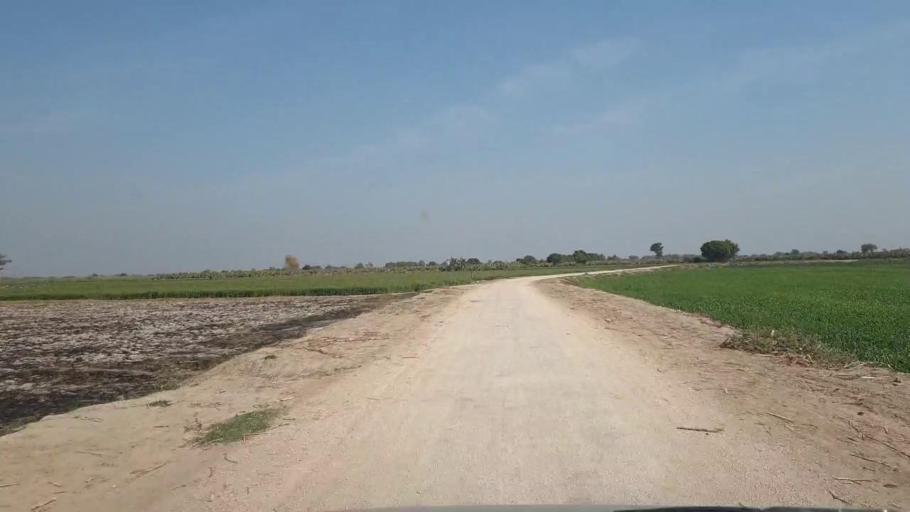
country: PK
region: Sindh
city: Chambar
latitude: 25.3485
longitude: 68.8332
